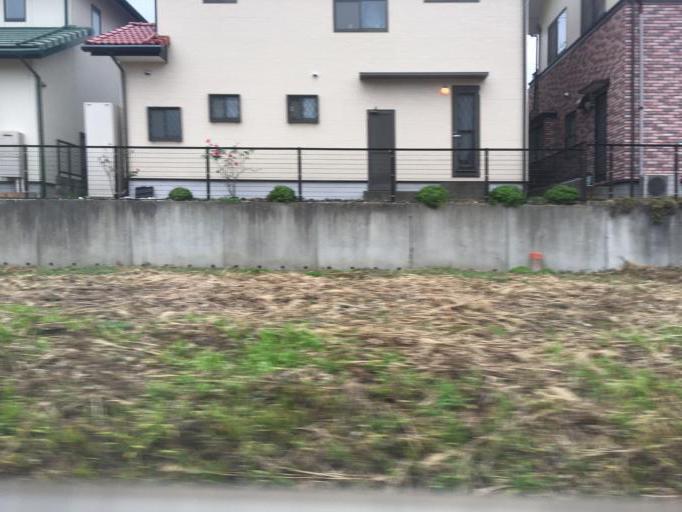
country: JP
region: Tochigi
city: Oyama
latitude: 36.3302
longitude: 139.8083
